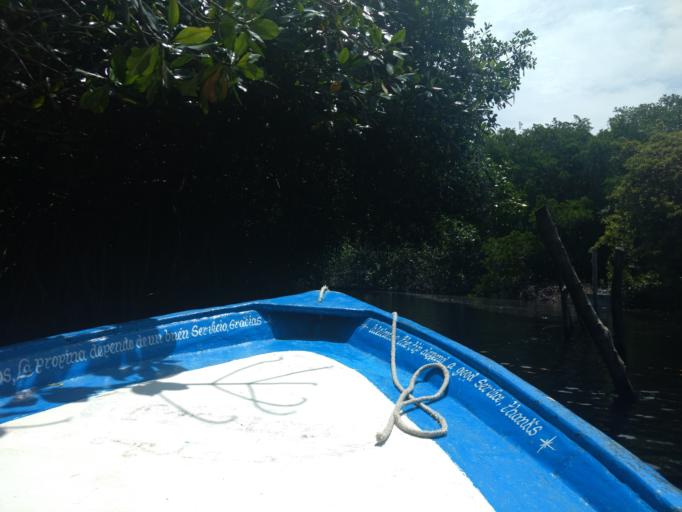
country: MX
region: Nayarit
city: San Blas
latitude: 21.5320
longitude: -105.2472
